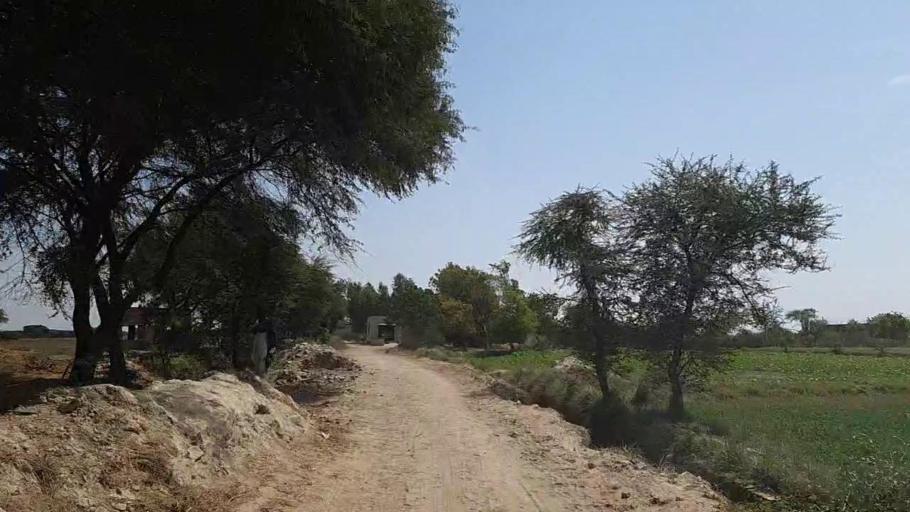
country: PK
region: Sindh
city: Mirpur Batoro
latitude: 24.7764
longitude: 68.2412
